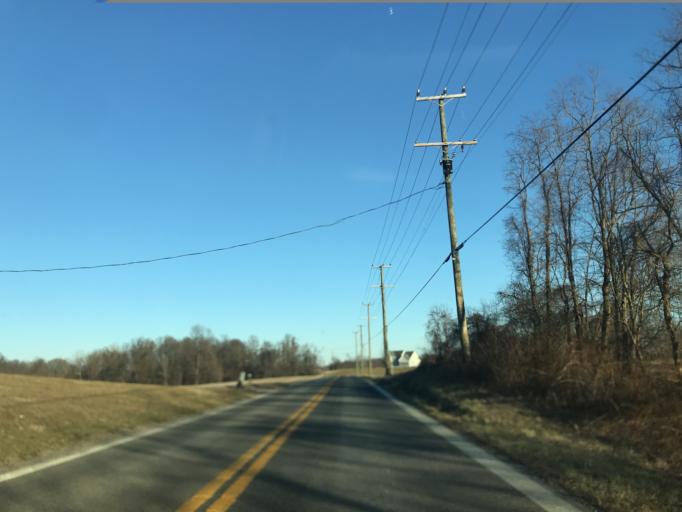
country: US
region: Maryland
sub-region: Prince George's County
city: Marlboro Meadows
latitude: 38.8384
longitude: -76.6472
